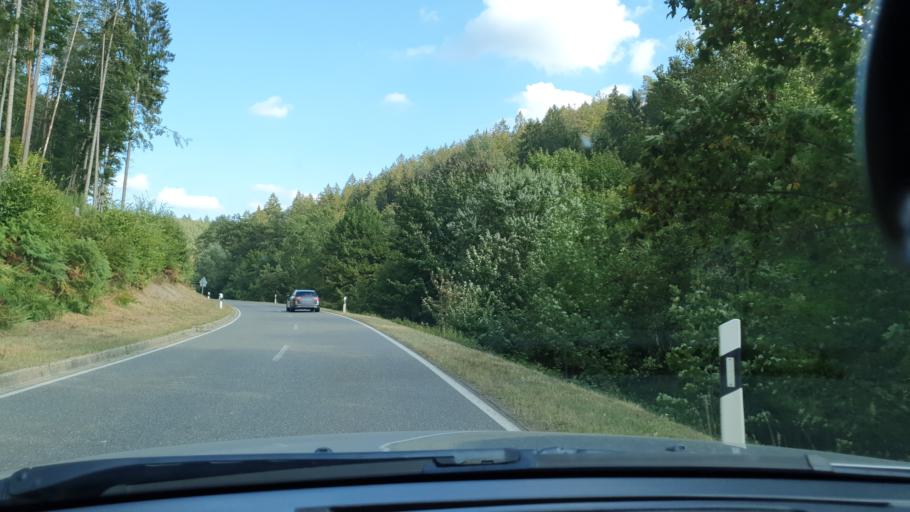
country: DE
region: Rheinland-Pfalz
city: Stelzenberg
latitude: 49.3686
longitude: 7.7192
